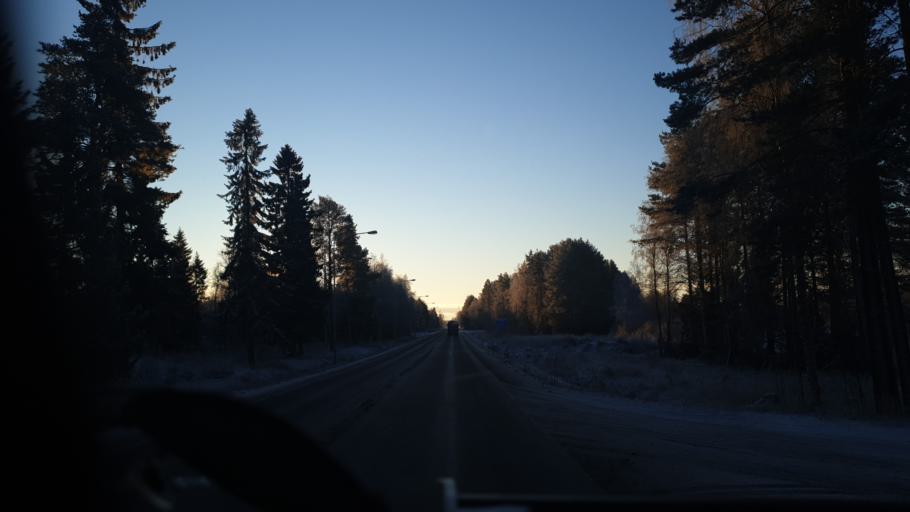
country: FI
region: Northern Ostrobothnia
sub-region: Ylivieska
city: Kalajoki
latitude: 64.2750
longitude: 23.9488
